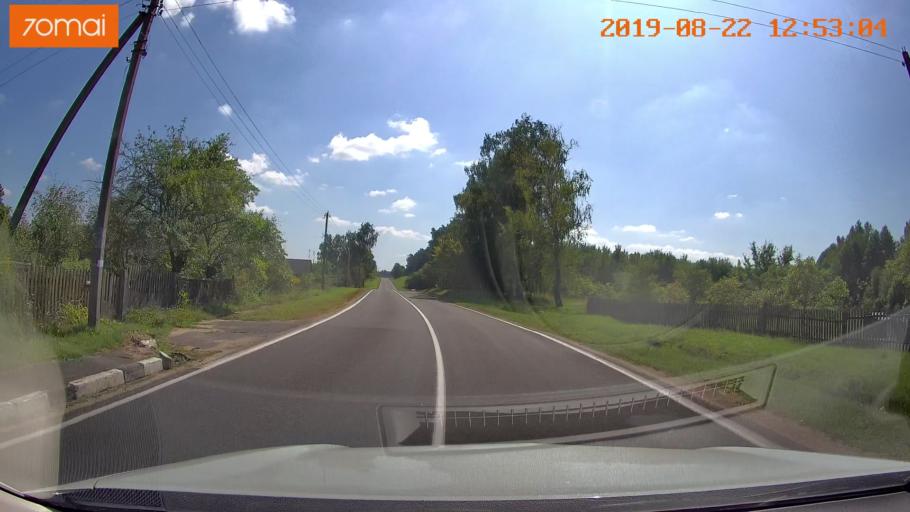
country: BY
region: Minsk
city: Prawdzinski
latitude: 53.4501
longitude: 27.6821
